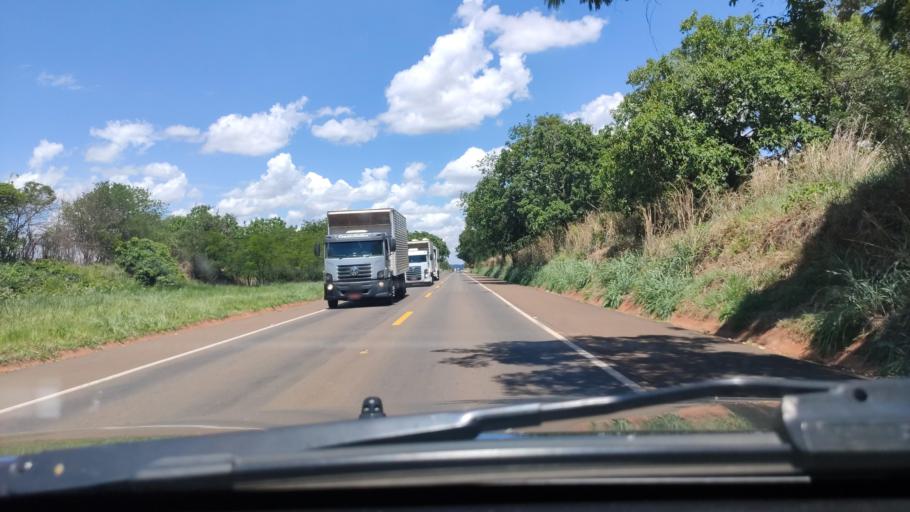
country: BR
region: Sao Paulo
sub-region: Boa Esperanca Do Sul
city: Boa Esperanca do Sul
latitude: -22.0694
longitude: -48.3989
